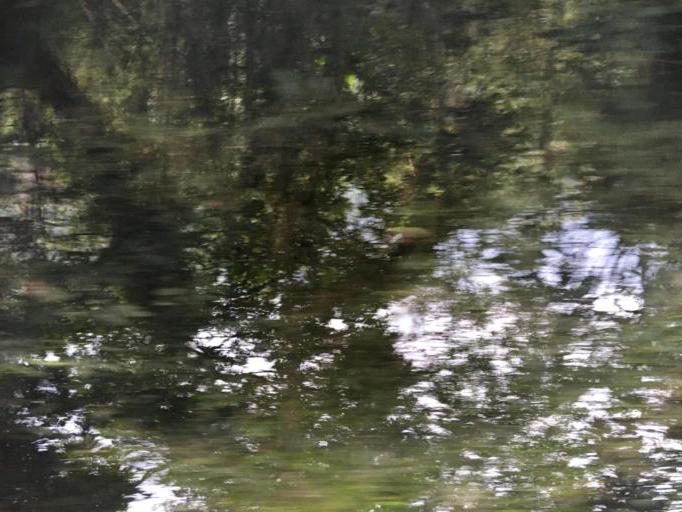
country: TW
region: Taiwan
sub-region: Chiayi
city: Jiayi Shi
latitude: 23.5380
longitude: 120.6274
